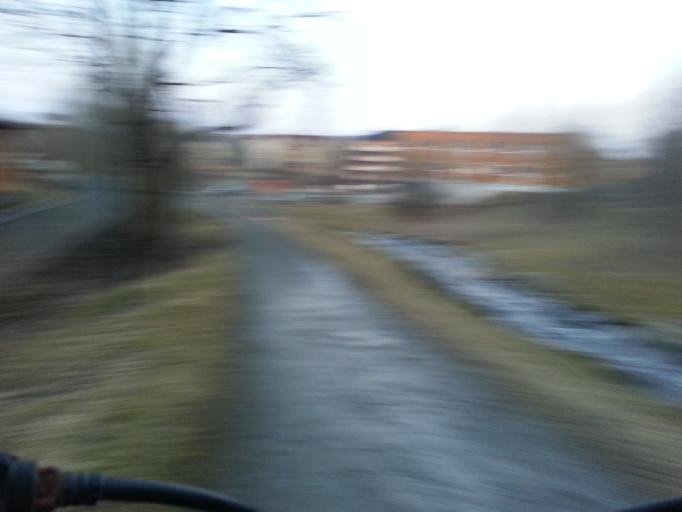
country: NO
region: Sor-Trondelag
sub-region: Trondheim
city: Trondheim
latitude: 63.4293
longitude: 10.3629
